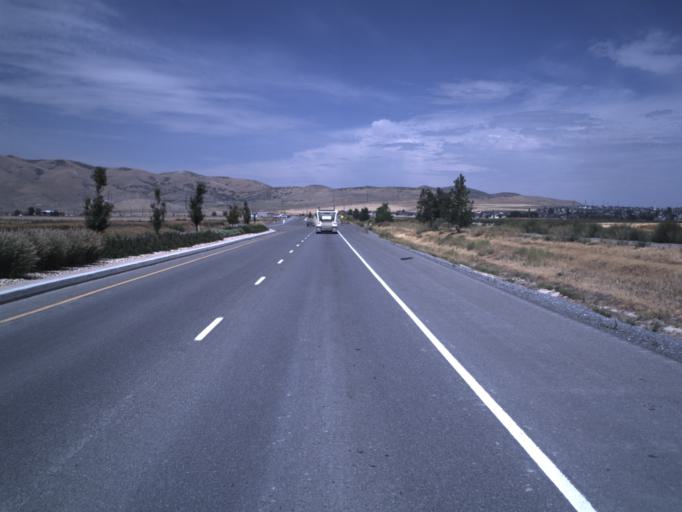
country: US
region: Utah
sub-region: Utah County
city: Saratoga Springs
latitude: 40.3777
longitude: -111.9249
